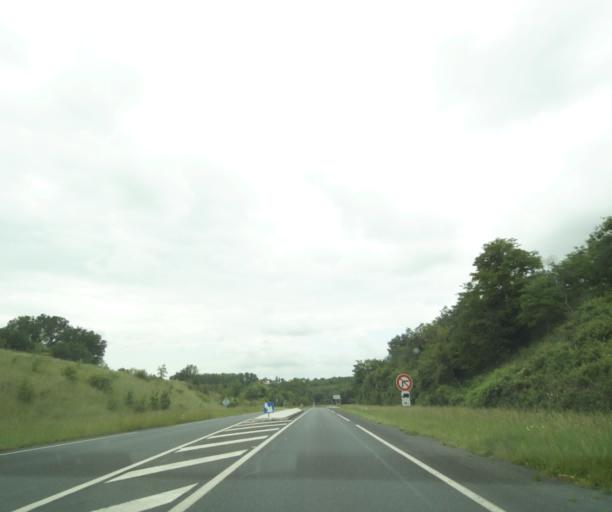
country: FR
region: Poitou-Charentes
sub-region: Departement des Deux-Sevres
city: Saint-Varent
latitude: 46.9121
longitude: -0.1946
